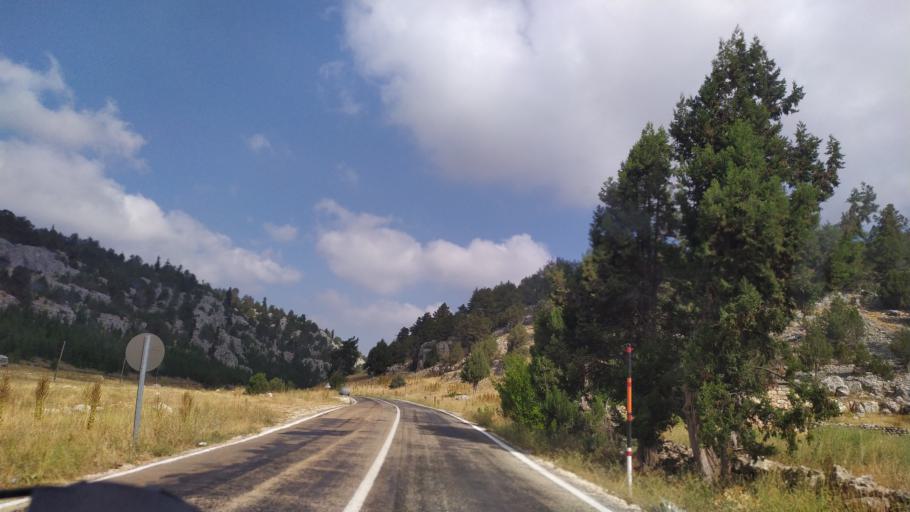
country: TR
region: Mersin
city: Kirobasi
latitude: 36.6147
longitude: 33.8780
